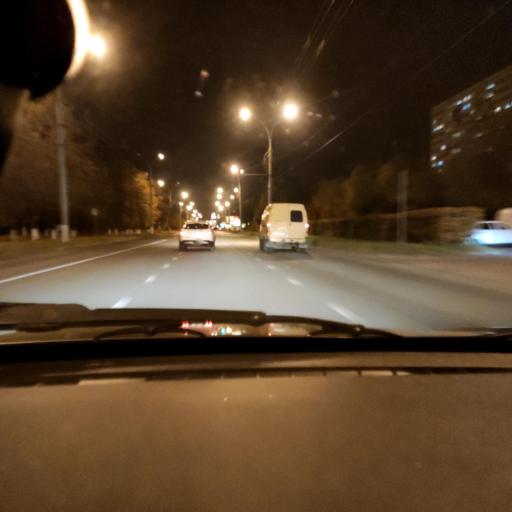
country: RU
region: Samara
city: Tol'yatti
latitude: 53.5233
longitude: 49.2747
